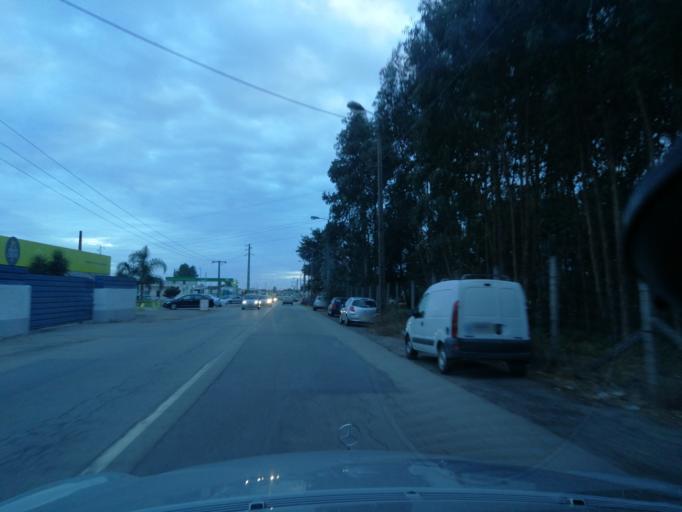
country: PT
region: Aveiro
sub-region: Estarreja
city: Beduido
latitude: 40.7728
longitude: -8.5692
